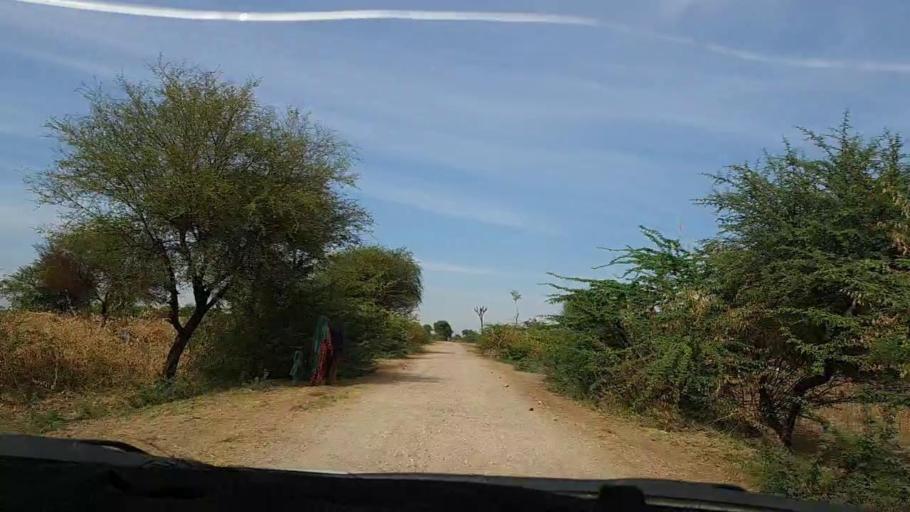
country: PK
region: Sindh
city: Pithoro
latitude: 25.4889
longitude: 69.4701
